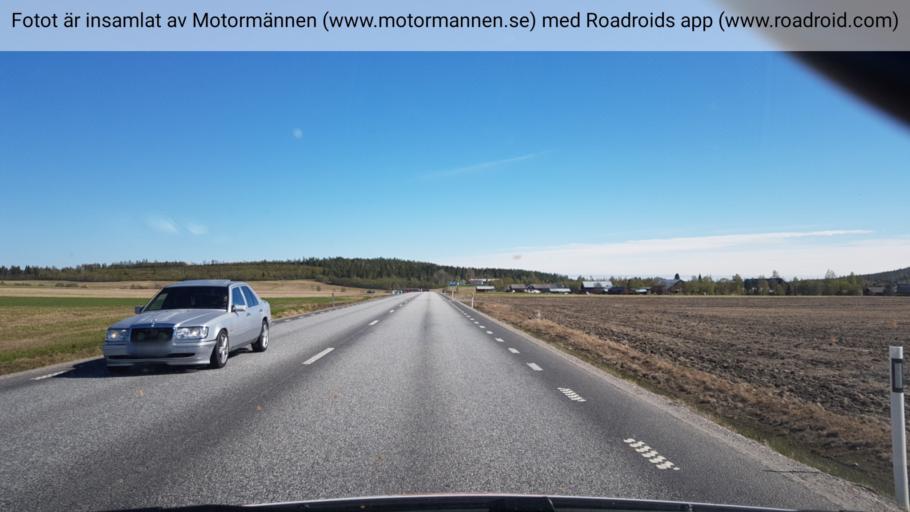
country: SE
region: Vaesterbotten
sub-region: Umea Kommun
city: Roback
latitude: 63.8705
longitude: 20.0739
